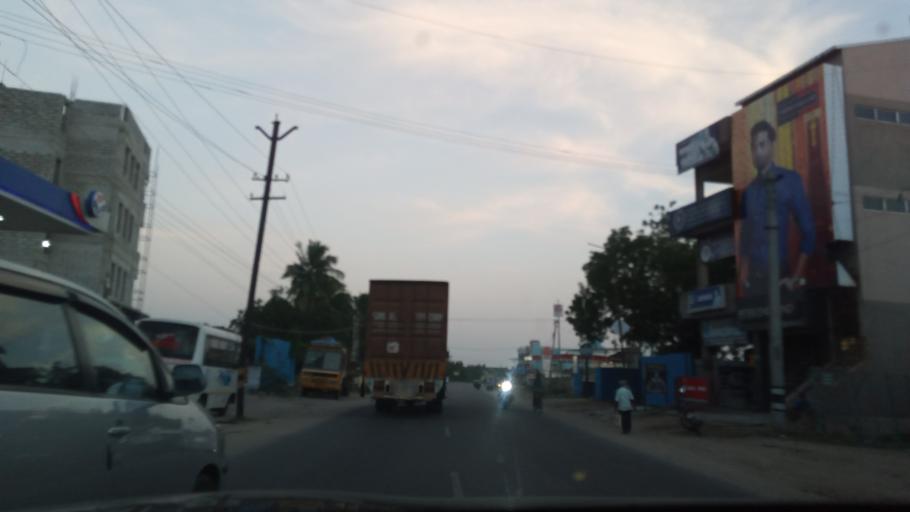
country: IN
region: Tamil Nadu
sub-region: Vellore
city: Walajapet
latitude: 12.9314
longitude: 79.3368
